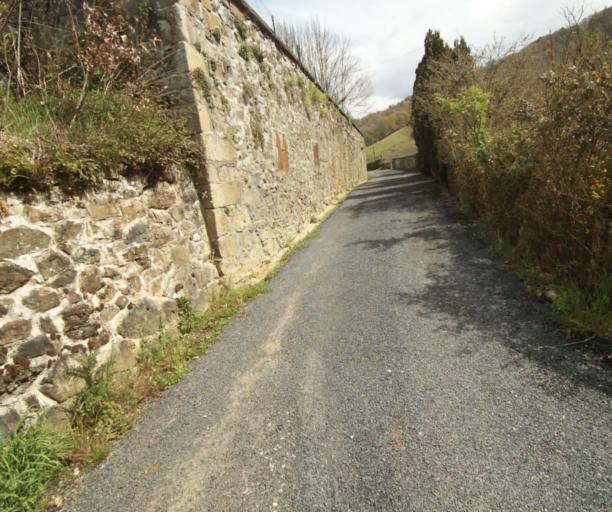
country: FR
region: Limousin
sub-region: Departement de la Correze
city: Tulle
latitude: 45.2735
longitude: 1.8004
